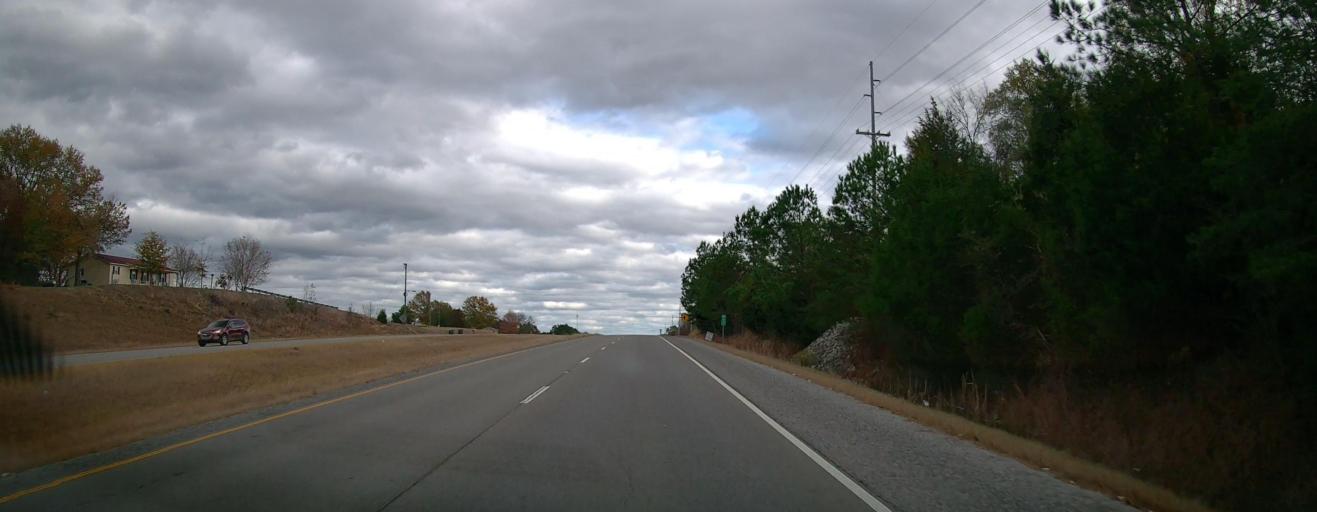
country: US
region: Alabama
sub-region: Lawrence County
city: Moulton
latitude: 34.5630
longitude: -87.3561
